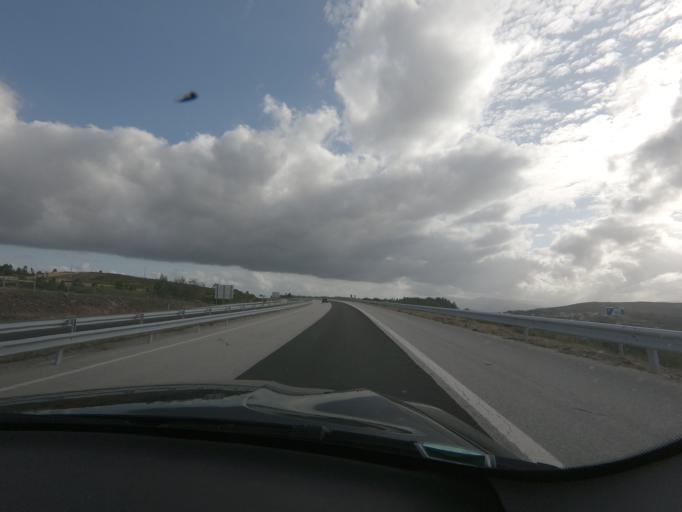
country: PT
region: Viseu
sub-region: Castro Daire
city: Castro Daire
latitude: 40.9459
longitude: -7.9023
